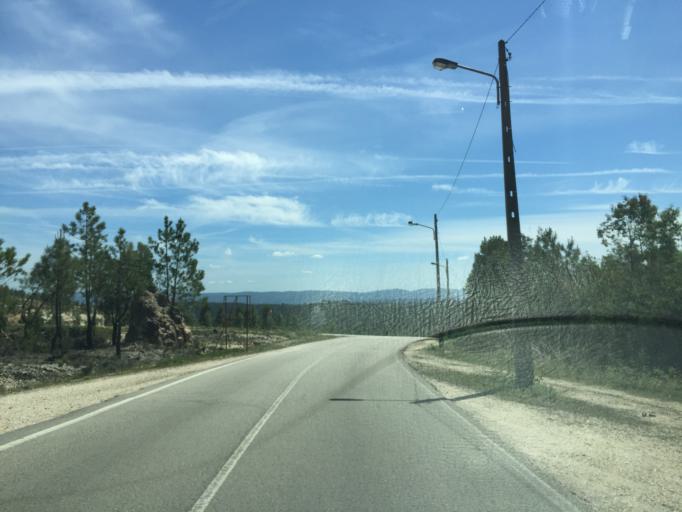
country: PT
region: Coimbra
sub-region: Soure
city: Soure
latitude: 40.0618
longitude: -8.6867
